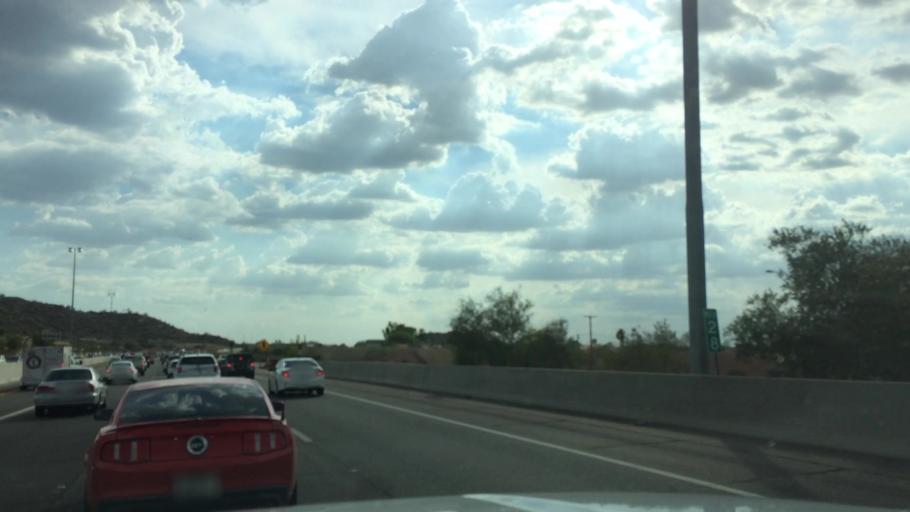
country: US
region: Arizona
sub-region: Maricopa County
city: Paradise Valley
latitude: 33.6720
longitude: -112.0350
